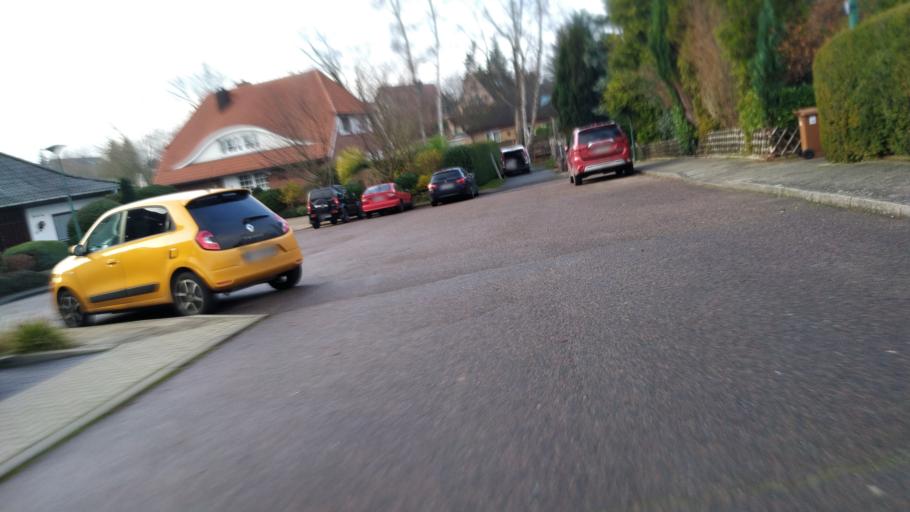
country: DE
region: Schleswig-Holstein
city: Travemuende
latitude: 53.9638
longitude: 10.8685
